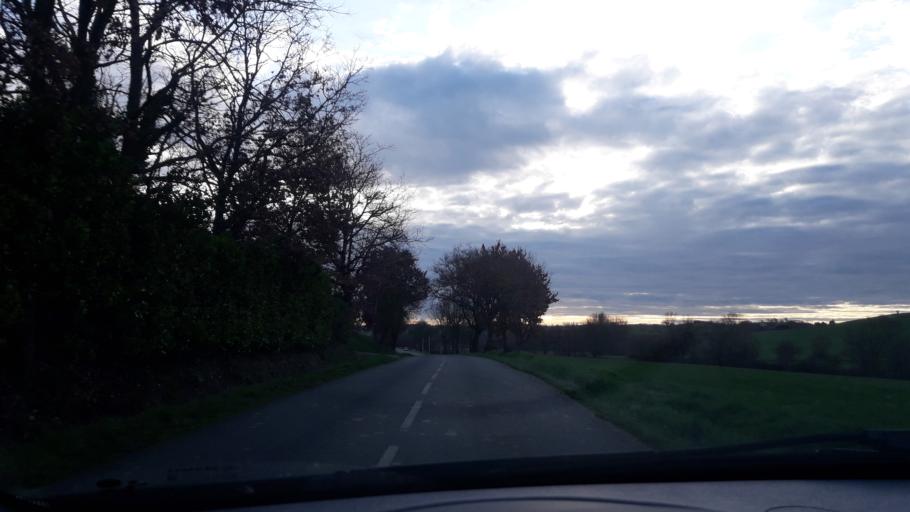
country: FR
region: Midi-Pyrenees
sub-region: Departement du Gers
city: Pujaudran
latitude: 43.6597
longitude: 1.1058
